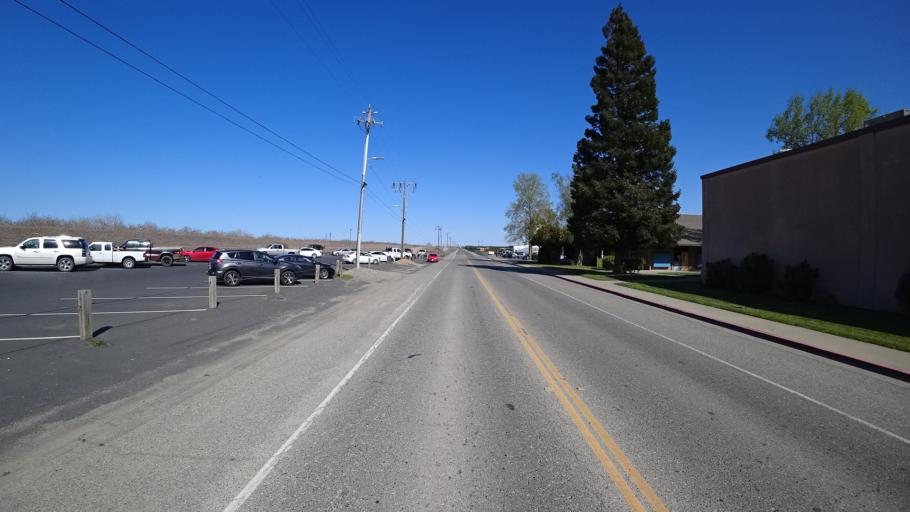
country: US
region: California
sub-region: Glenn County
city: Hamilton City
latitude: 39.7453
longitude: -122.0198
